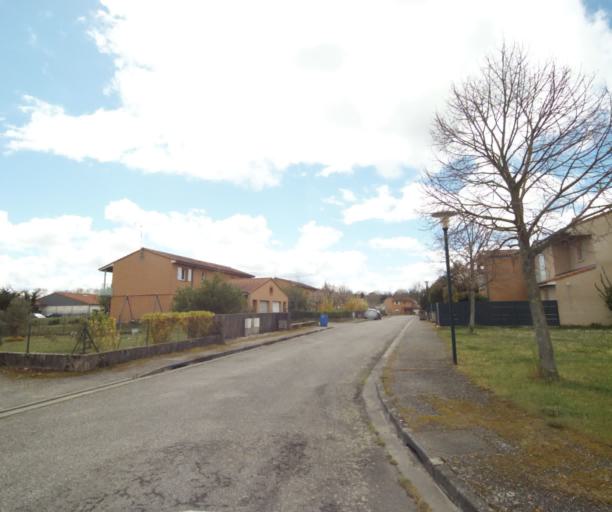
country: FR
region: Midi-Pyrenees
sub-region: Departement de l'Ariege
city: Saverdun
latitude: 43.2346
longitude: 1.5846
